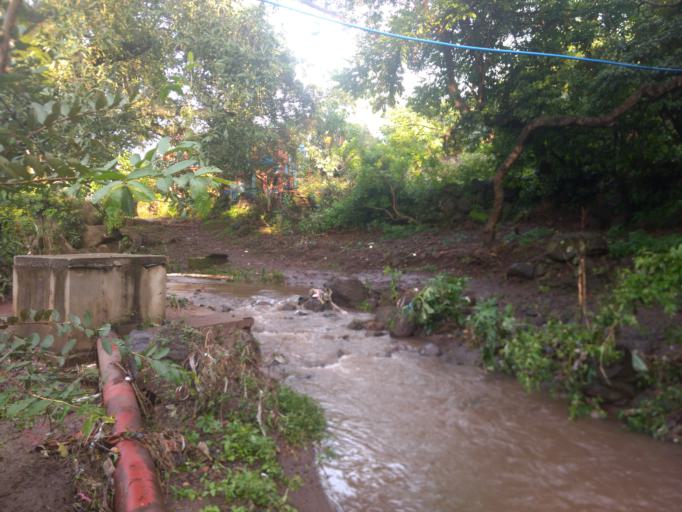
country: MX
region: Nayarit
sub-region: Tepic
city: La Corregidora
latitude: 21.4614
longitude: -104.8047
